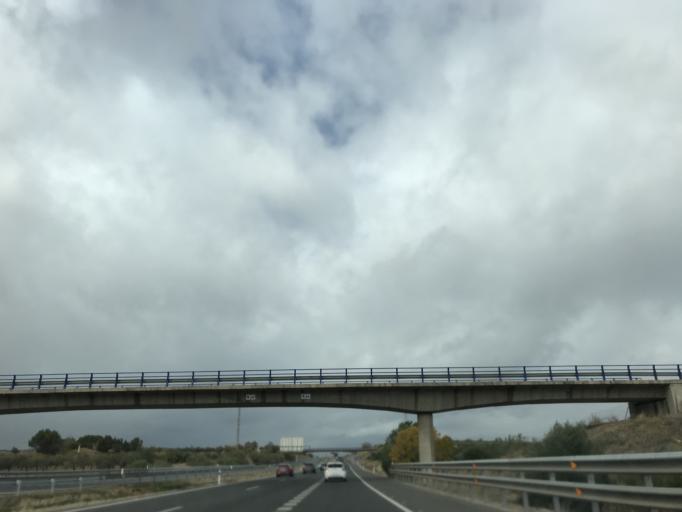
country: ES
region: Andalusia
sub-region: Provincia de Jaen
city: Bailen
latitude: 38.1023
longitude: -3.7427
